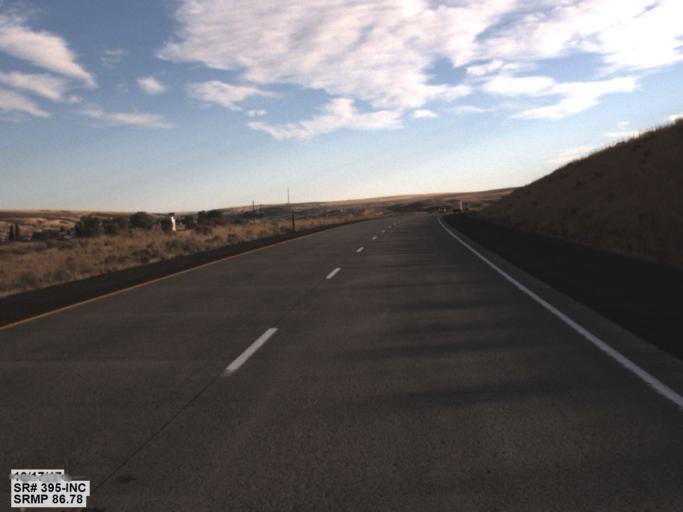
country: US
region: Washington
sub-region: Adams County
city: Ritzville
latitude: 47.0157
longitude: -118.5012
